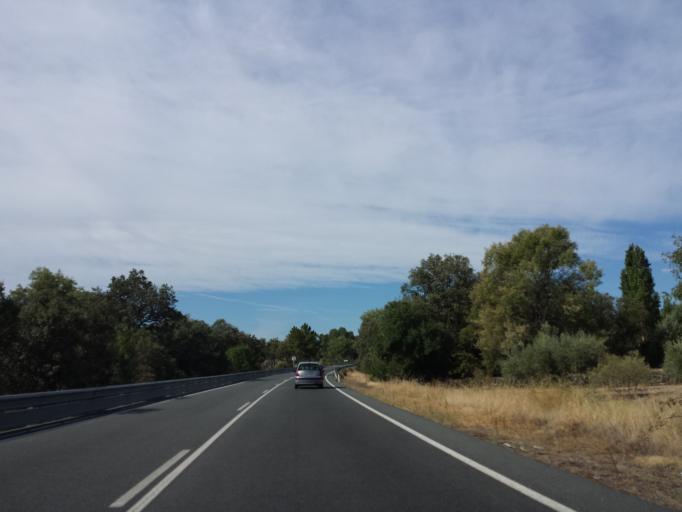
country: ES
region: Castille and Leon
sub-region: Provincia de Avila
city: Casavieja
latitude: 40.2763
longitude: -4.7402
